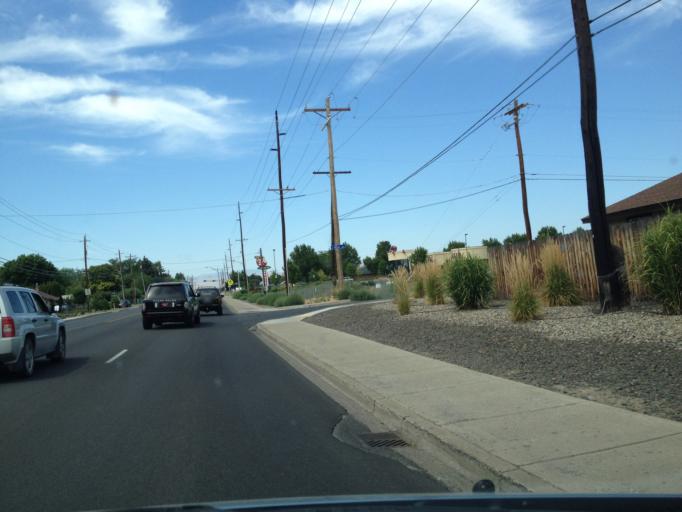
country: US
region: Washington
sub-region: Yakima County
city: West Valley
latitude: 46.5855
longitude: -120.5638
